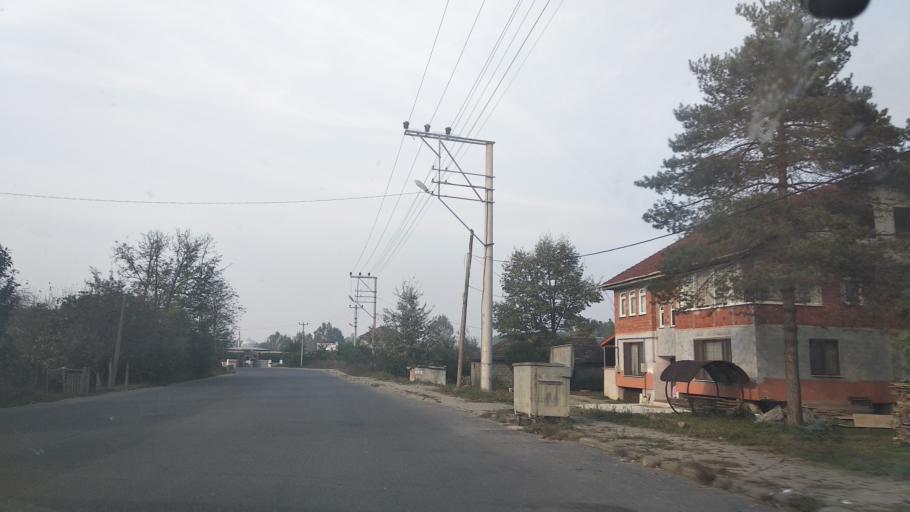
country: TR
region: Duzce
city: Duzce
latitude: 40.8092
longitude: 31.1786
